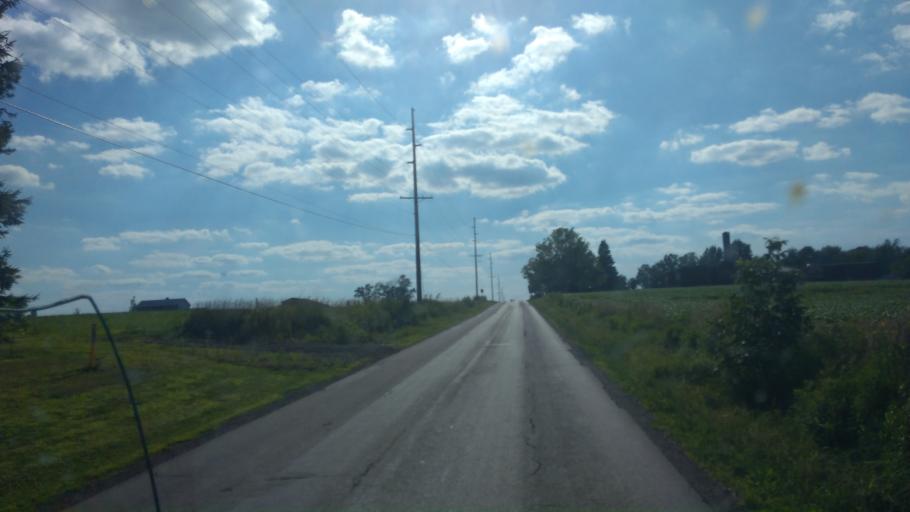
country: US
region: Ohio
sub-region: Wayne County
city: Apple Creek
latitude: 40.7111
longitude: -81.9183
